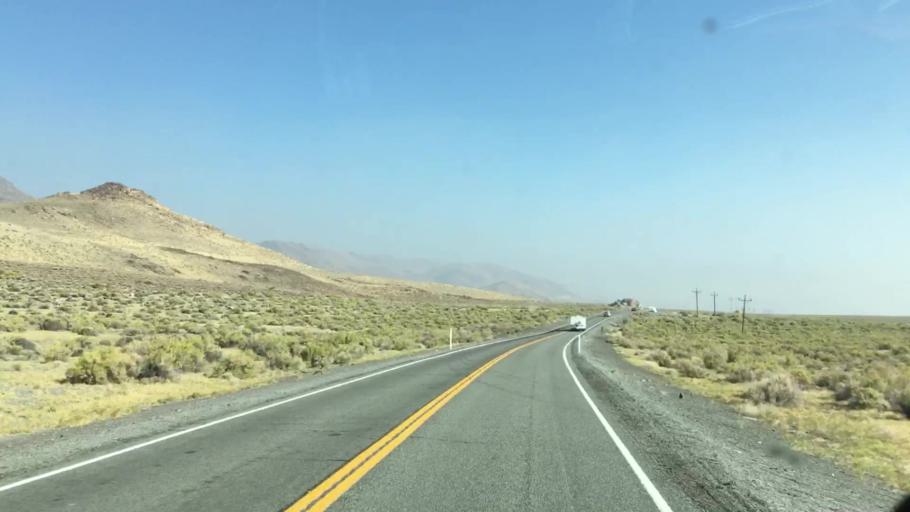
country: US
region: Nevada
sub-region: Lyon County
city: Fernley
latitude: 40.1848
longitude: -119.3700
